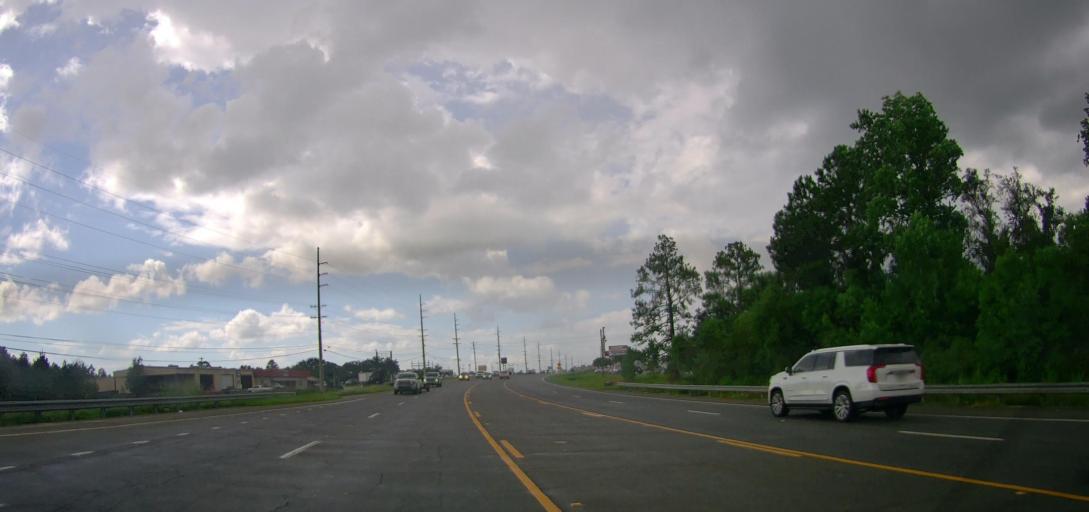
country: US
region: Georgia
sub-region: Coffee County
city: Douglas
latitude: 31.4910
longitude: -82.8693
